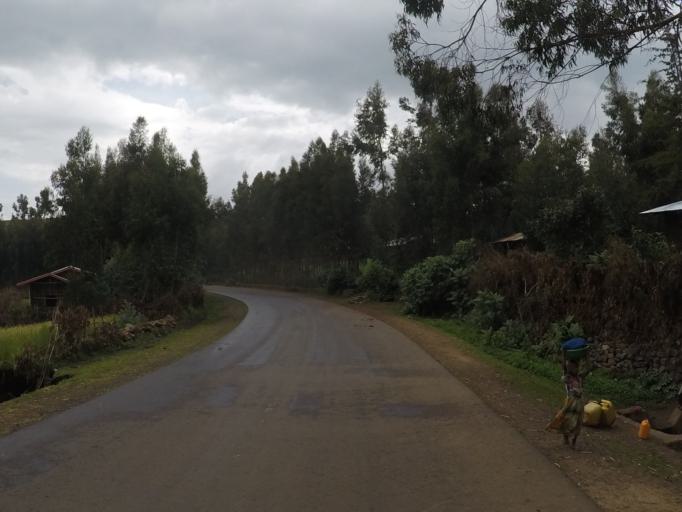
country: ET
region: Amhara
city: Dabat
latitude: 13.0591
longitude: 37.8222
